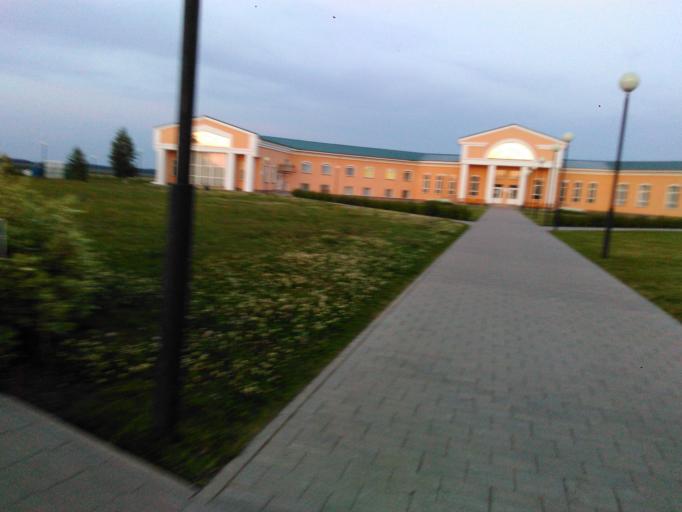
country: RU
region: Penza
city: Lermontovo
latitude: 53.0002
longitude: 43.6715
